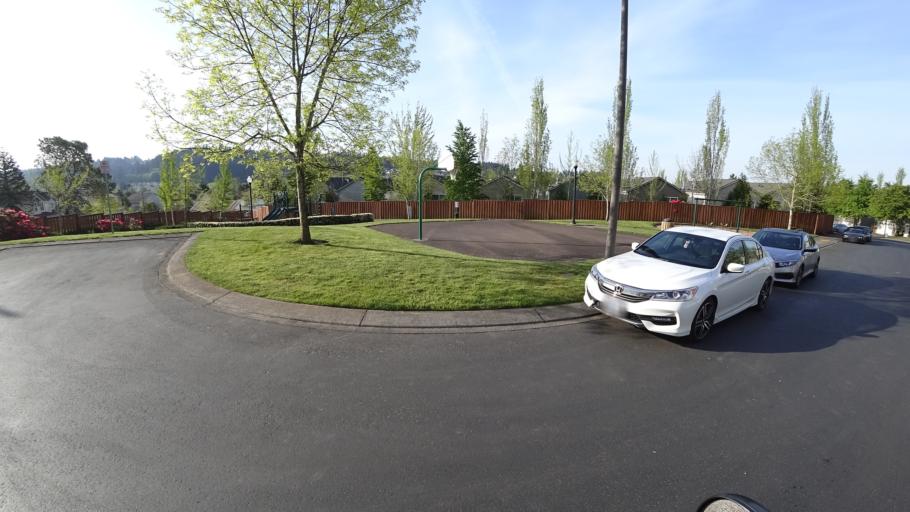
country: US
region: Oregon
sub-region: Washington County
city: King City
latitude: 45.4289
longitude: -122.8434
